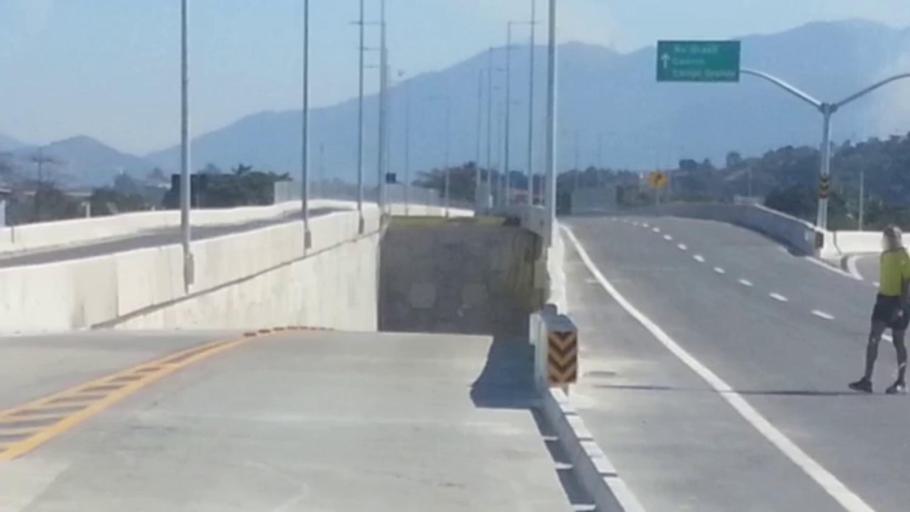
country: BR
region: Rio de Janeiro
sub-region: Nilopolis
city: Nilopolis
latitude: -22.8710
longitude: -43.4113
